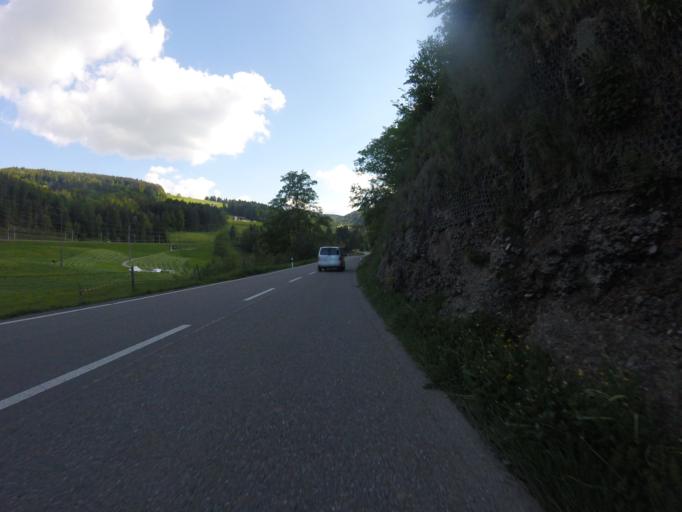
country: CH
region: Saint Gallen
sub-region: Wahlkreis Wil
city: Degersheim
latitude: 47.3648
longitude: 9.1862
